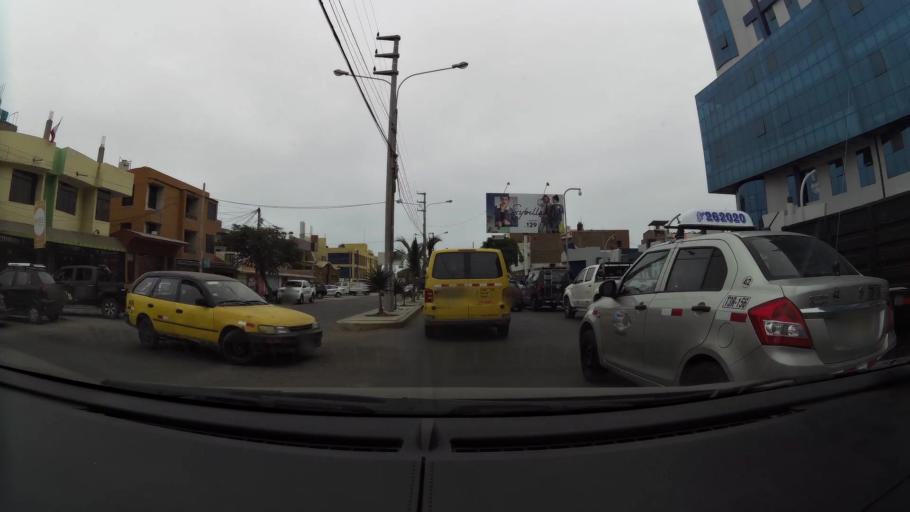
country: PE
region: La Libertad
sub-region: Provincia de Trujillo
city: Buenos Aires
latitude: -8.1300
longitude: -79.0436
